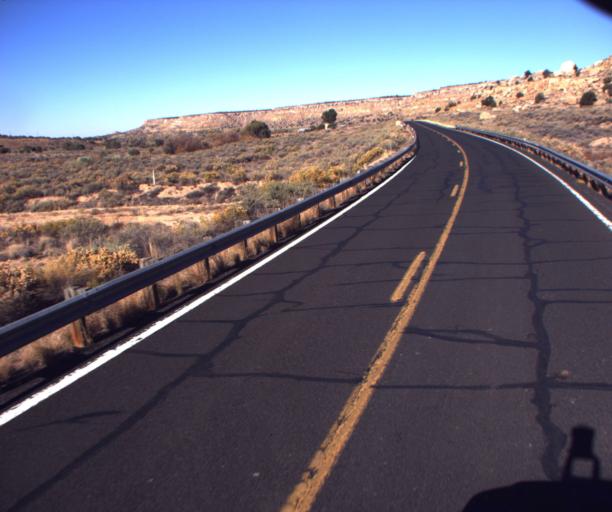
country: US
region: Arizona
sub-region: Navajo County
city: First Mesa
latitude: 35.8389
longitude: -110.2326
